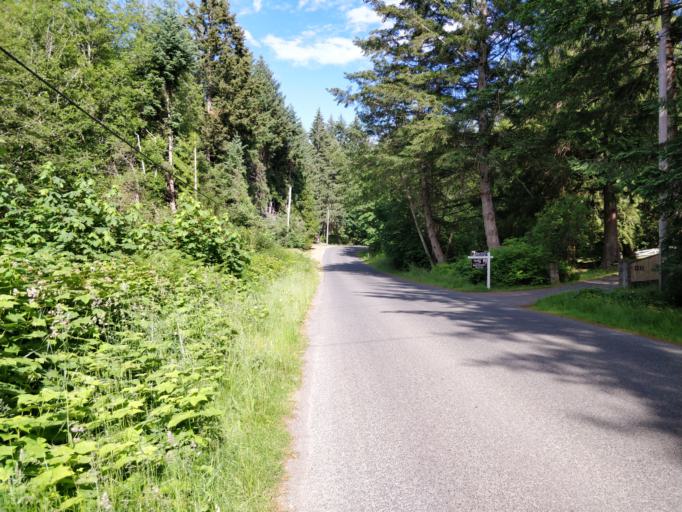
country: CA
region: British Columbia
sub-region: Cowichan Valley Regional District
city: Ladysmith
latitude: 49.0791
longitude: -123.7976
